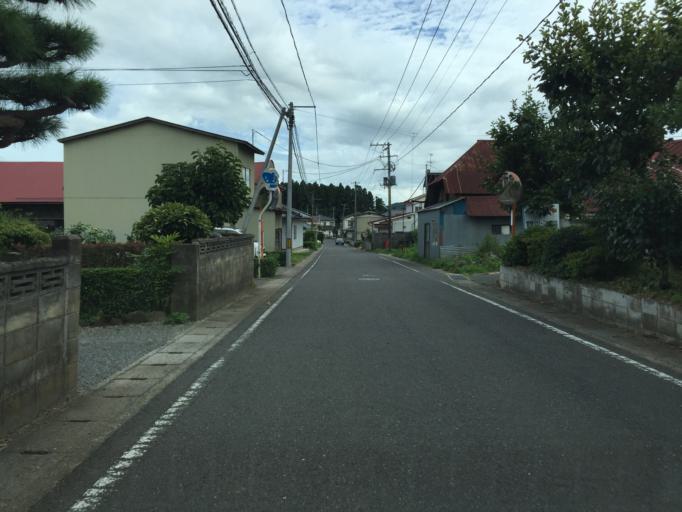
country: JP
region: Fukushima
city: Motomiya
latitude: 37.5345
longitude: 140.3635
